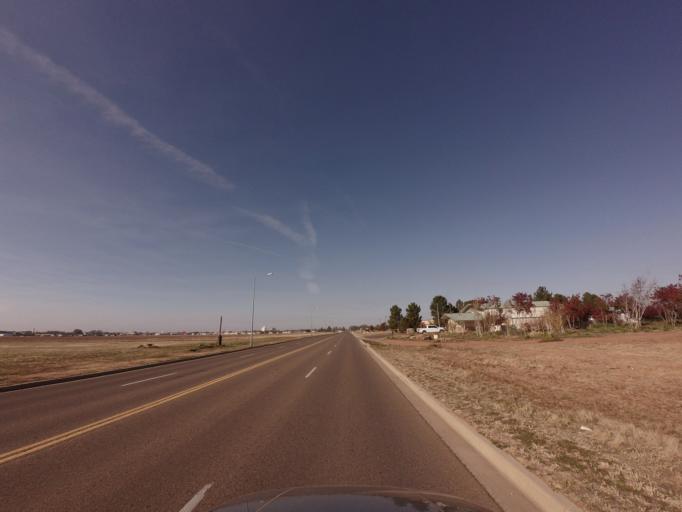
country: US
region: New Mexico
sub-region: Curry County
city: Clovis
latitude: 34.4049
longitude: -103.1692
